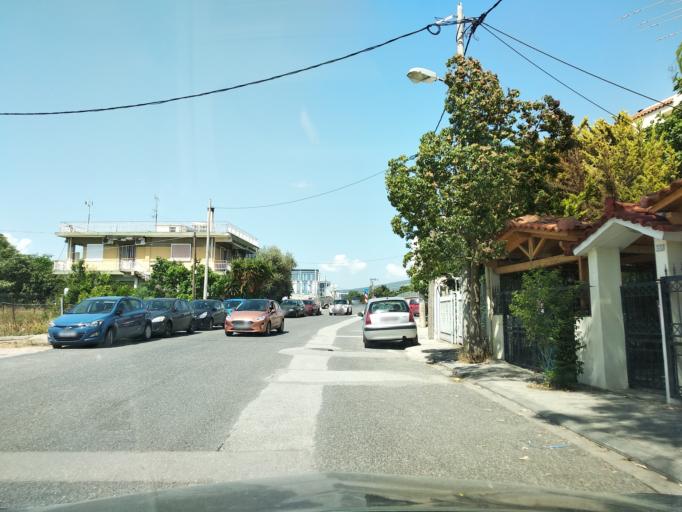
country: GR
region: Attica
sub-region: Nomarchia Athinas
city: Marousi
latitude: 38.0420
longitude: 23.8004
